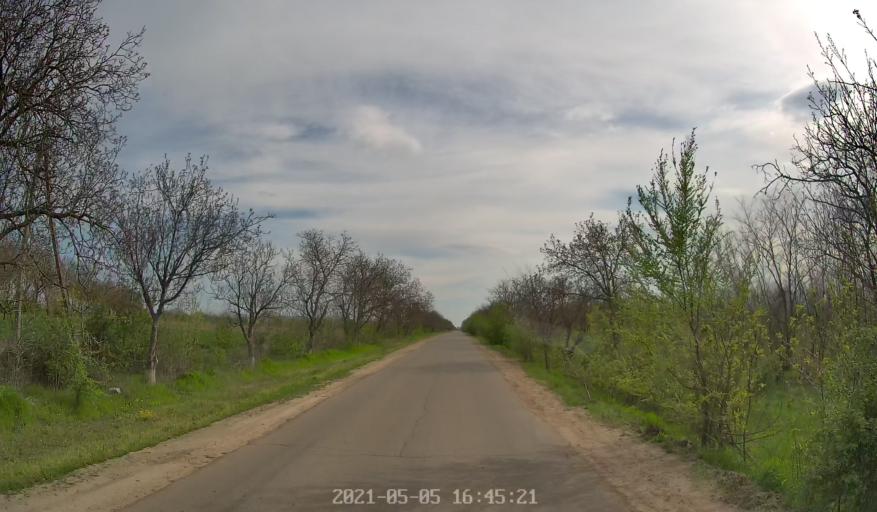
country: MD
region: Criuleni
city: Criuleni
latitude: 47.1105
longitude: 29.1936
